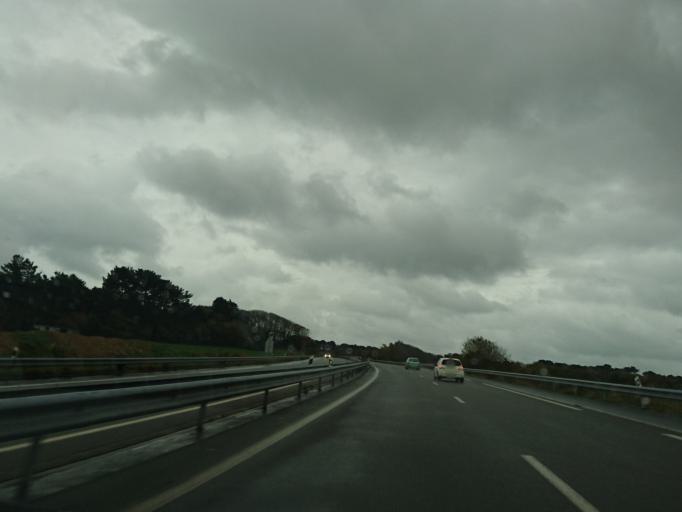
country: FR
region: Brittany
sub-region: Departement du Finistere
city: Guilers
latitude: 48.3901
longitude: -4.5479
